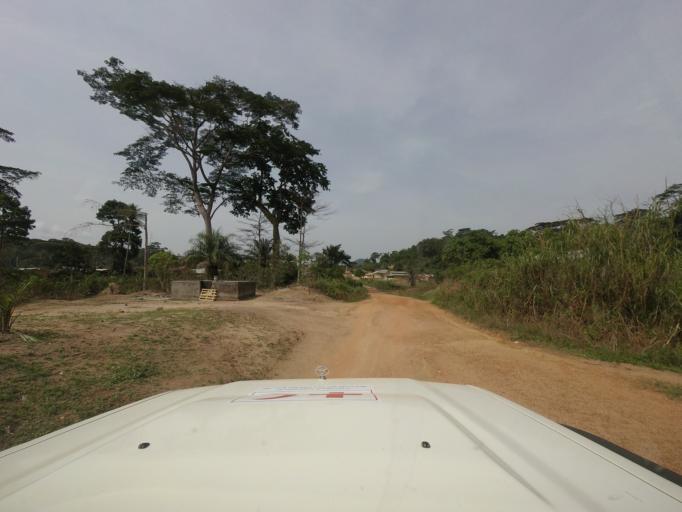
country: GN
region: Nzerekore
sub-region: Macenta
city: Macenta
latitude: 8.4584
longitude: -9.5851
